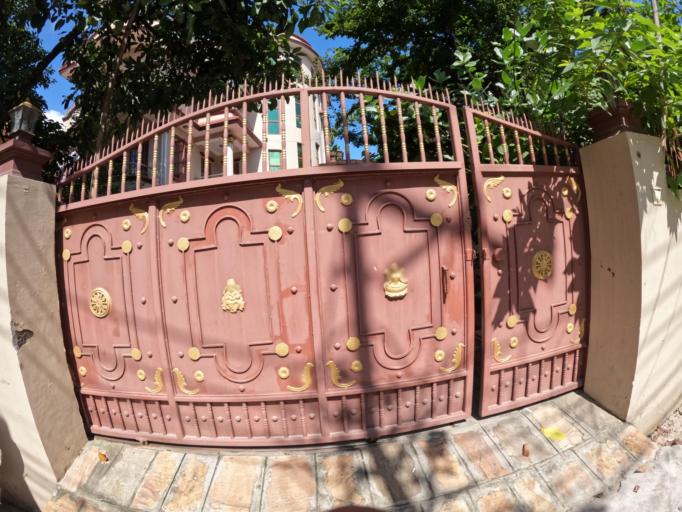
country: NP
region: Central Region
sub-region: Bagmati Zone
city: Kathmandu
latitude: 27.7494
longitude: 85.3329
